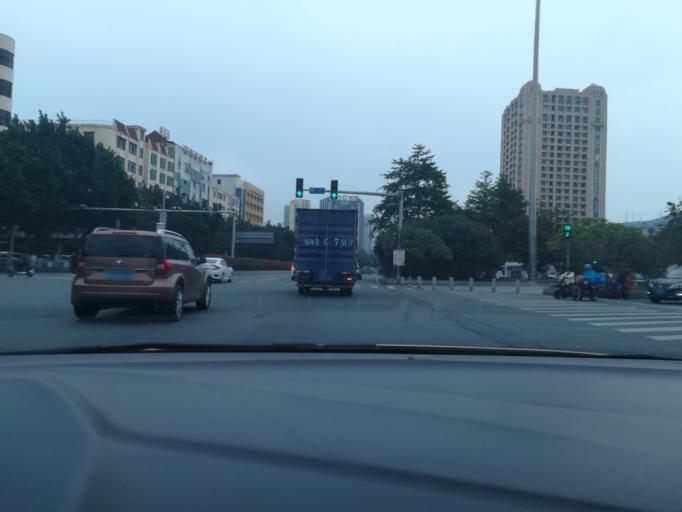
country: CN
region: Guangdong
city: Nansha
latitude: 22.8031
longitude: 113.5450
